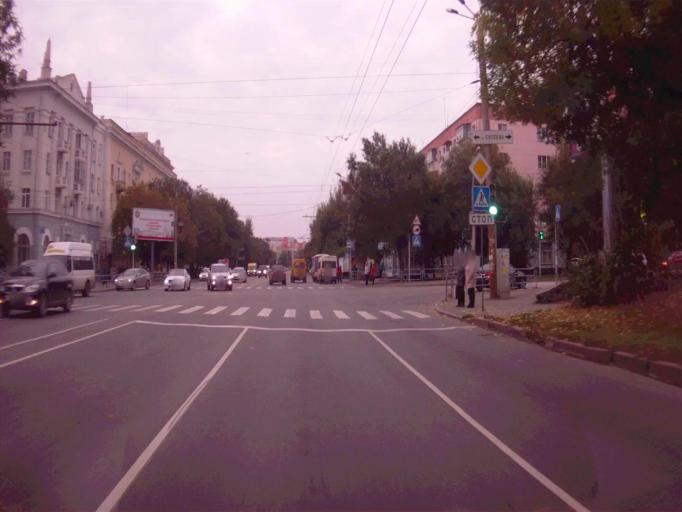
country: RU
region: Chelyabinsk
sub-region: Gorod Chelyabinsk
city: Chelyabinsk
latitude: 55.1506
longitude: 61.4154
